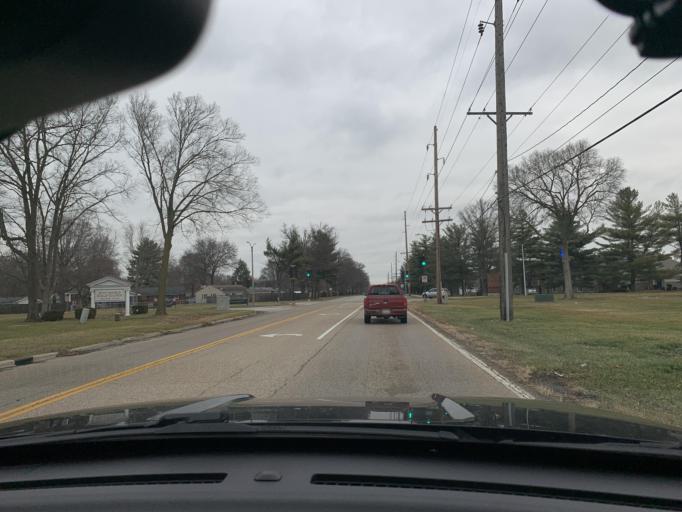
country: US
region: Illinois
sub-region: Sangamon County
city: Jerome
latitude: 39.7562
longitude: -89.6867
